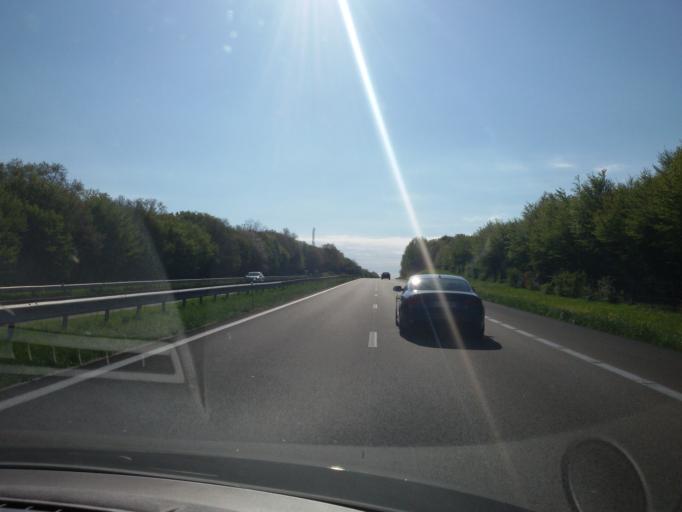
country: FR
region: Bourgogne
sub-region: Departement de l'Yonne
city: Joux-la-Ville
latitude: 47.6957
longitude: 3.8270
